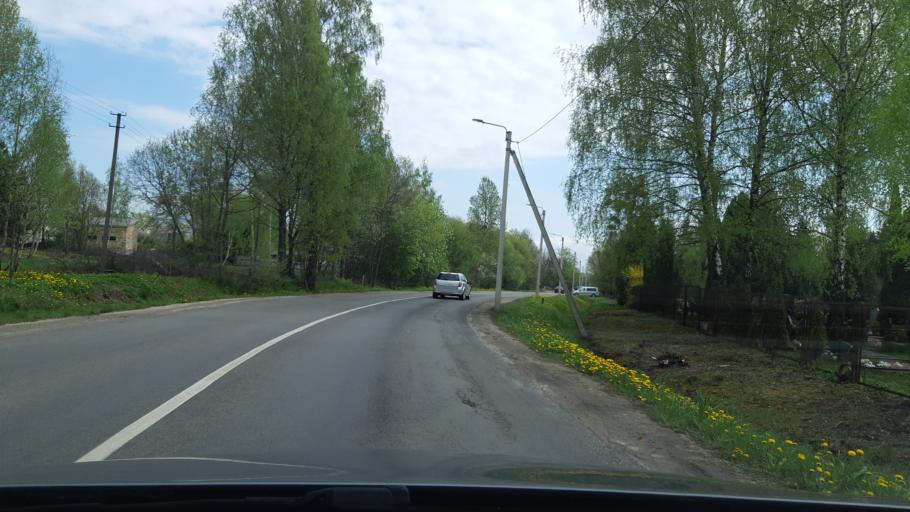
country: LT
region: Kauno apskritis
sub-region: Kaunas
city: Silainiai
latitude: 54.9238
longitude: 23.8495
